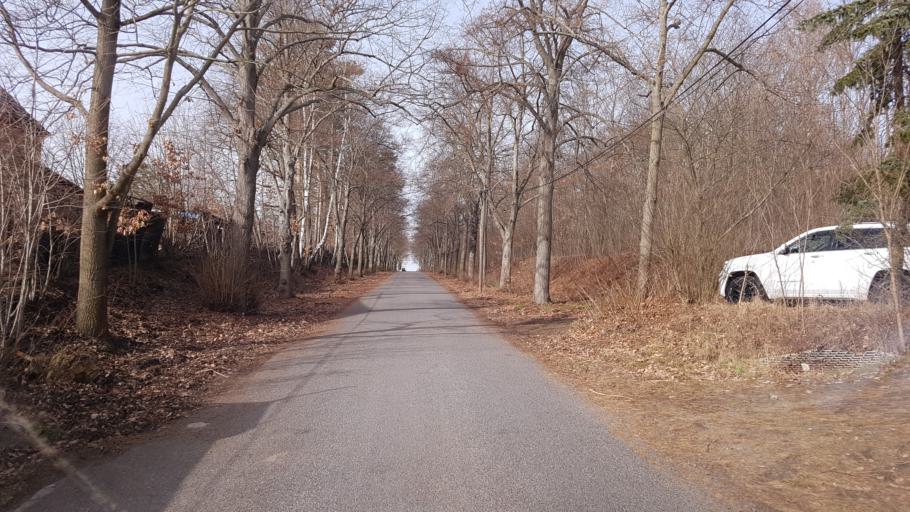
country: DE
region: Brandenburg
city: Schipkau
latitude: 51.5269
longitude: 13.8261
